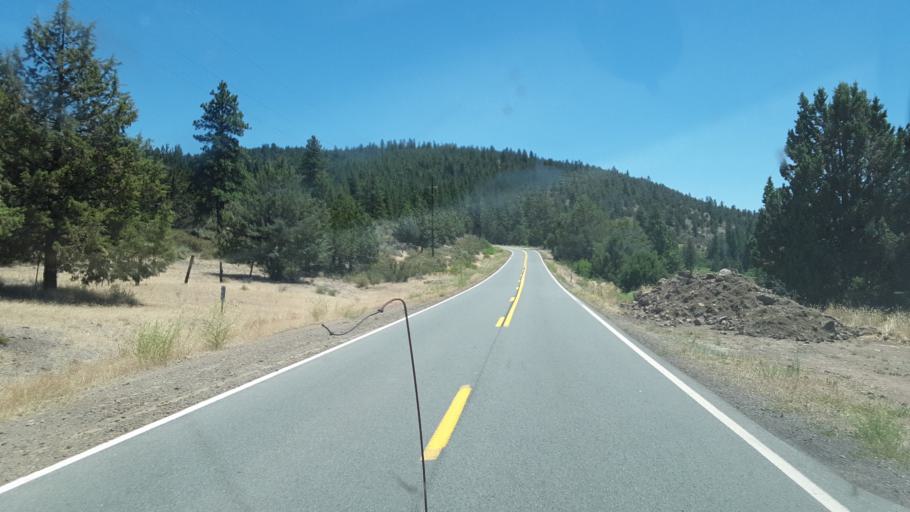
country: US
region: California
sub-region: Modoc County
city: Alturas
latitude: 41.0369
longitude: -120.8584
